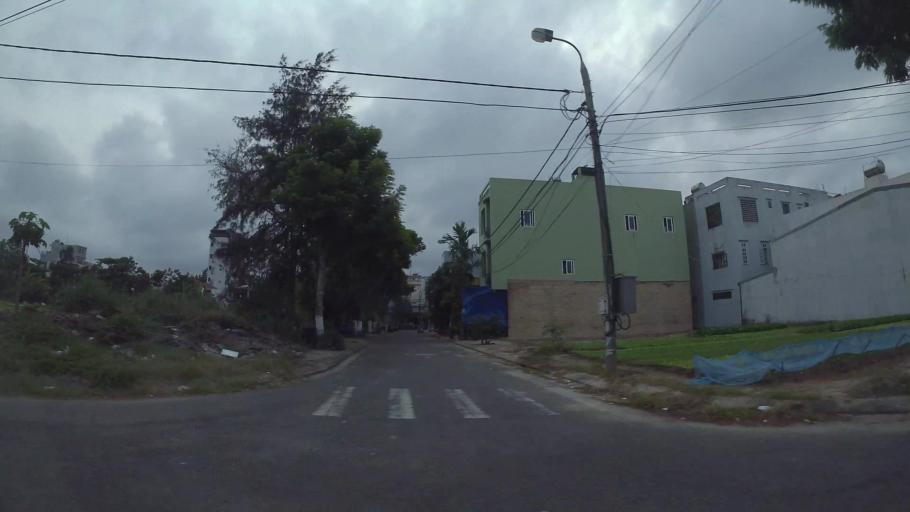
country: VN
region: Da Nang
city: Son Tra
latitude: 16.0481
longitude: 108.2357
